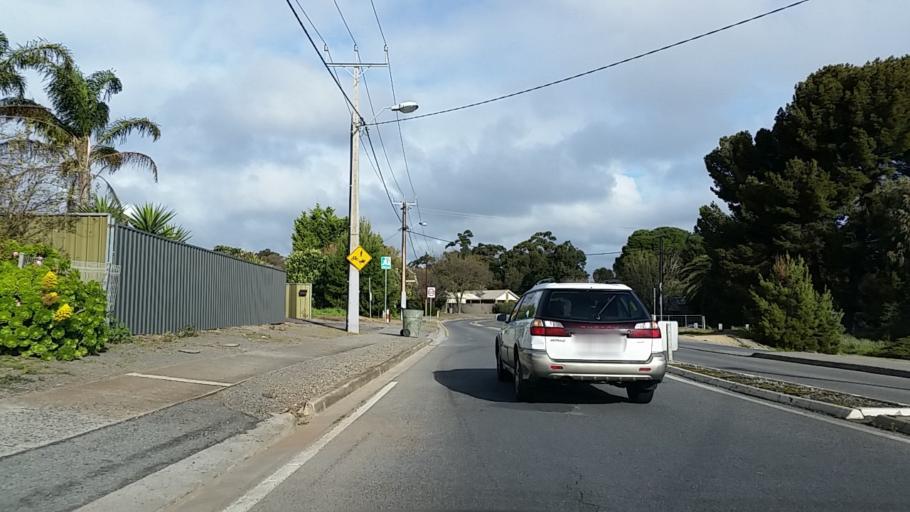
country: AU
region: South Australia
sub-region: Onkaparinga
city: Reynella
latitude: -35.0990
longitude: 138.5337
